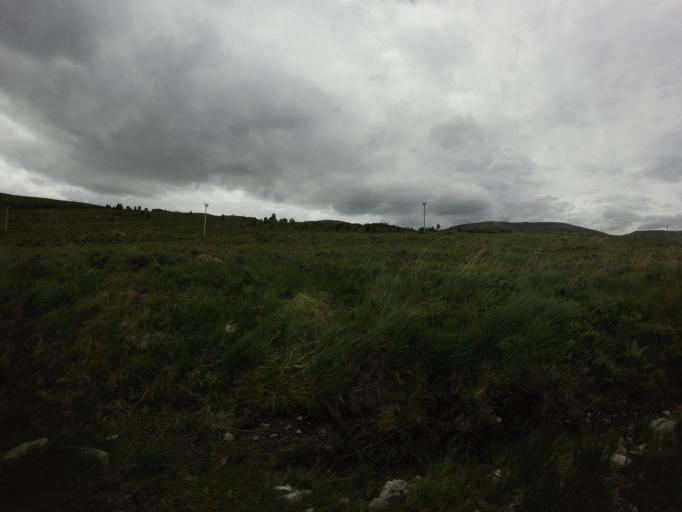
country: GB
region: Scotland
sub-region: Highland
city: Ullapool
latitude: 57.7046
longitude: -4.8239
